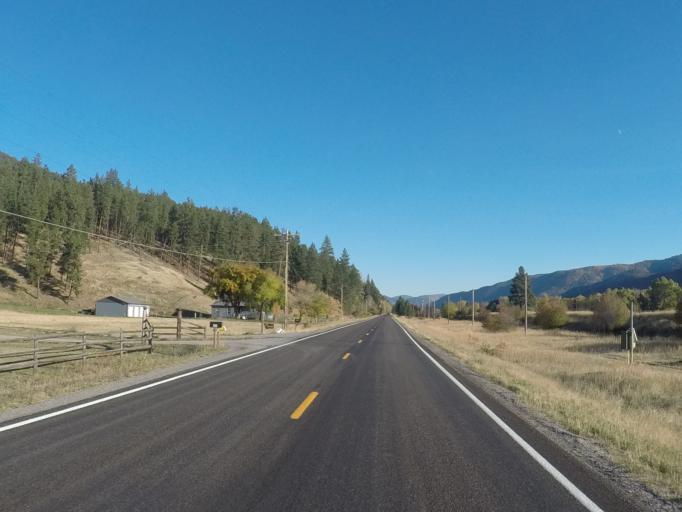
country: US
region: Montana
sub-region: Missoula County
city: Bonner-West Riverside
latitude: 46.8338
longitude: -113.8225
